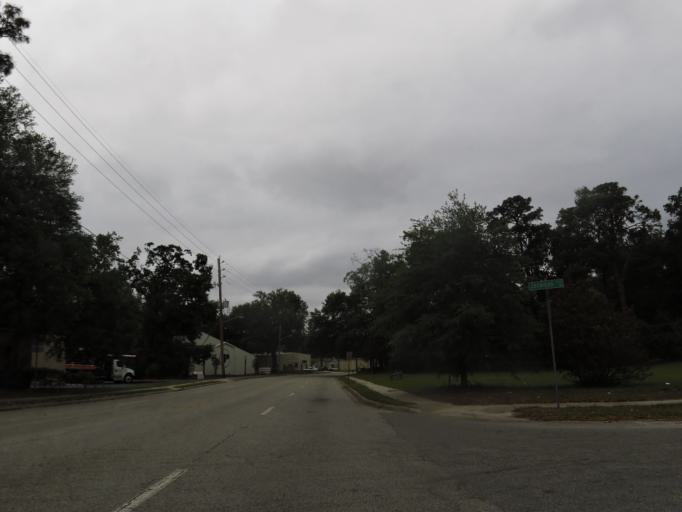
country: US
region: Florida
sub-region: Duval County
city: Jacksonville
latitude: 30.2770
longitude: -81.6425
